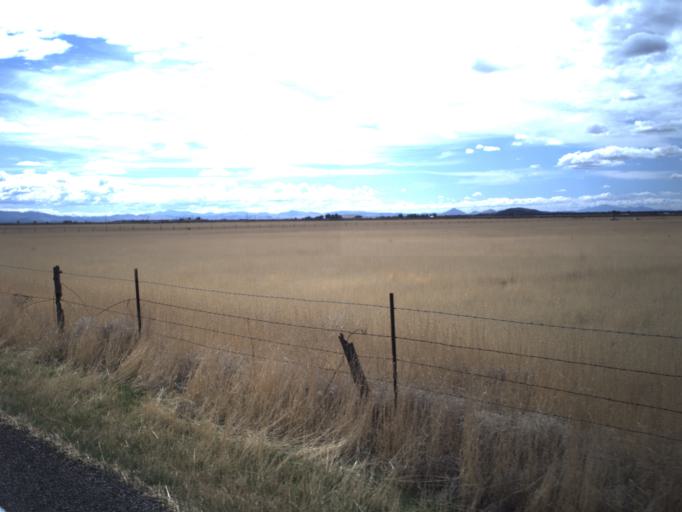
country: US
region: Utah
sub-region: Millard County
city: Fillmore
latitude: 39.0294
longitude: -112.4100
